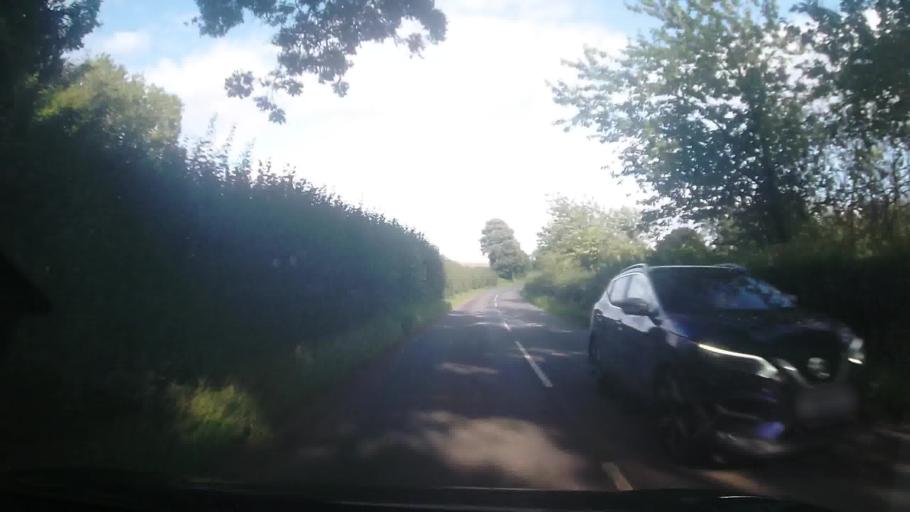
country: GB
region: England
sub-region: Shropshire
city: Bucknell
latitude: 52.4284
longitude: -2.9137
